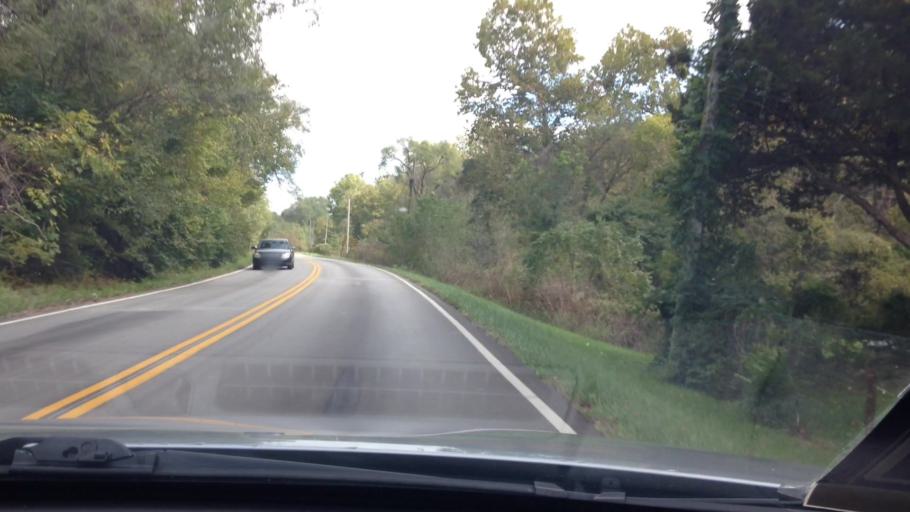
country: US
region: Missouri
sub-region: Platte County
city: Weatherby Lake
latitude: 39.2483
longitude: -94.7908
